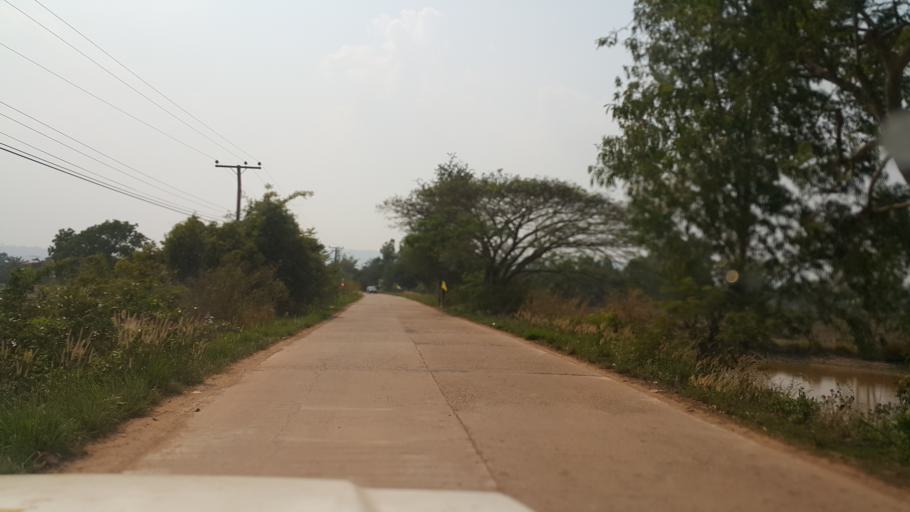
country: TH
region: Nakhon Phanom
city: Ban Phaeng
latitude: 17.9630
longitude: 104.1955
